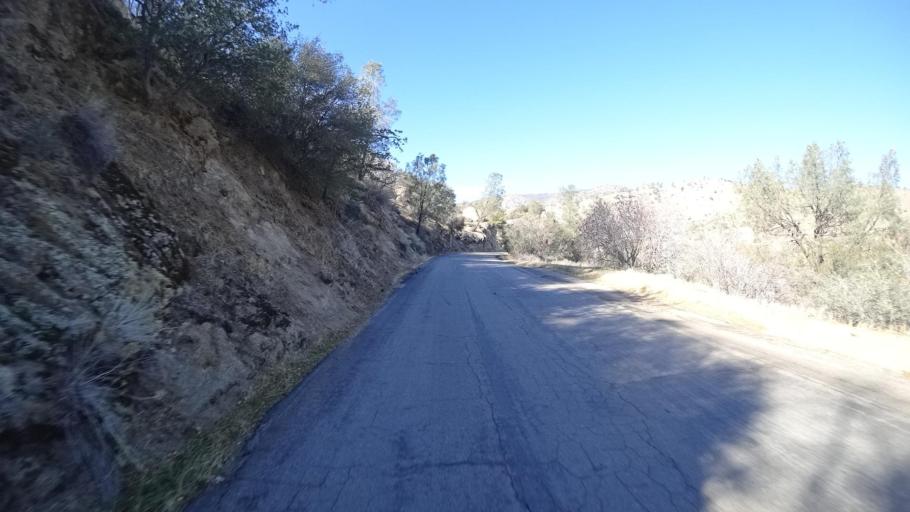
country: US
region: California
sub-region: Kern County
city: Bodfish
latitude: 35.5763
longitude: -118.5355
